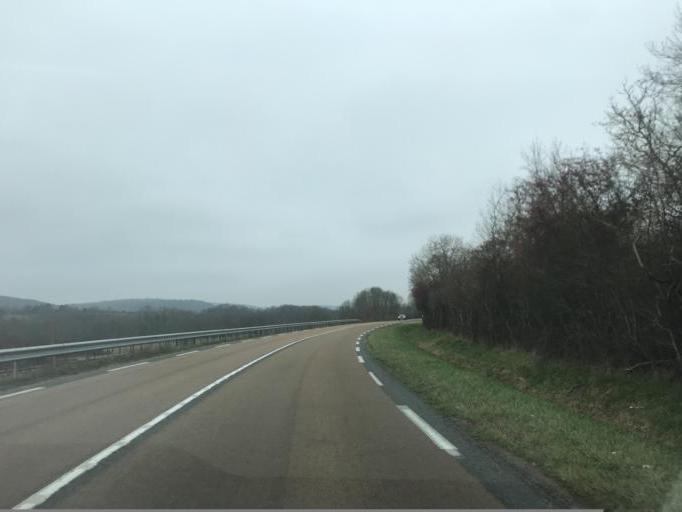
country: FR
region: Bourgogne
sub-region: Departement de l'Yonne
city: Avallon
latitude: 47.5145
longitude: 3.8178
